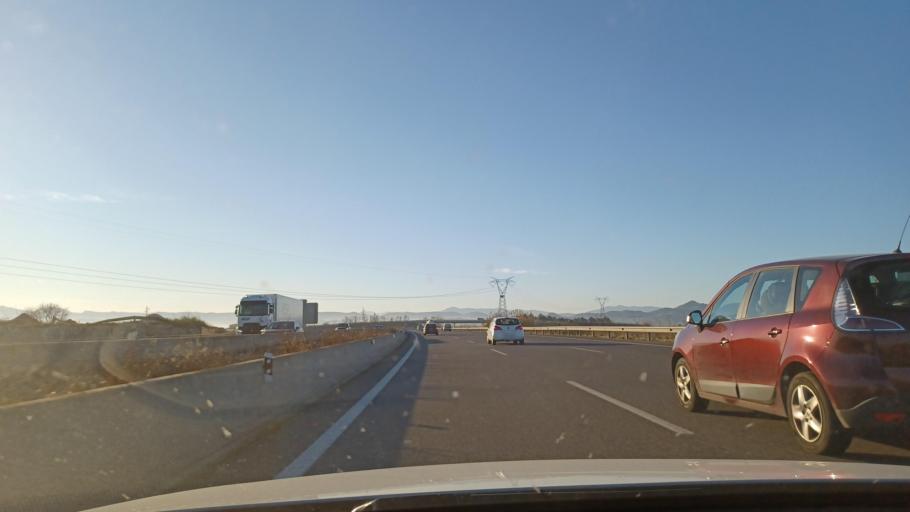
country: ES
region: Valencia
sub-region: Provincia de Valencia
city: Alberic
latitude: 39.1094
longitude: -0.5320
